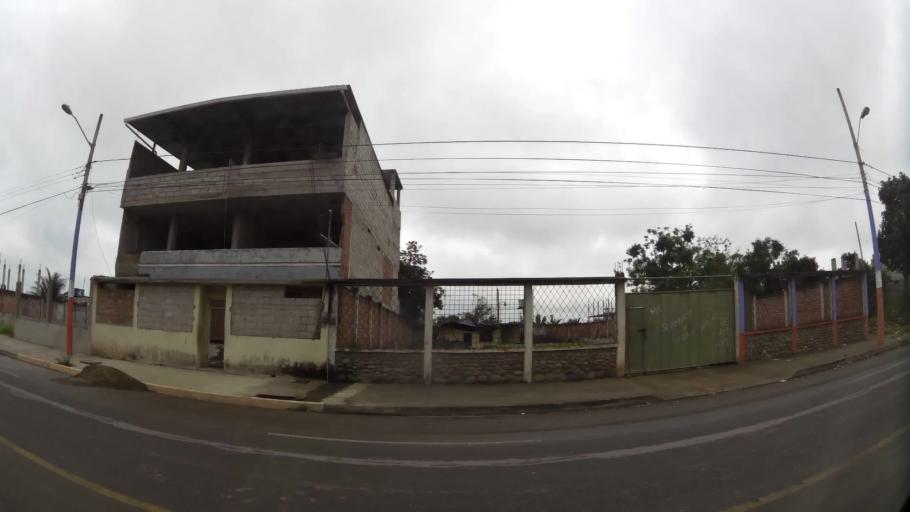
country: EC
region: El Oro
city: Pasaje
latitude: -3.3258
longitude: -79.8202
